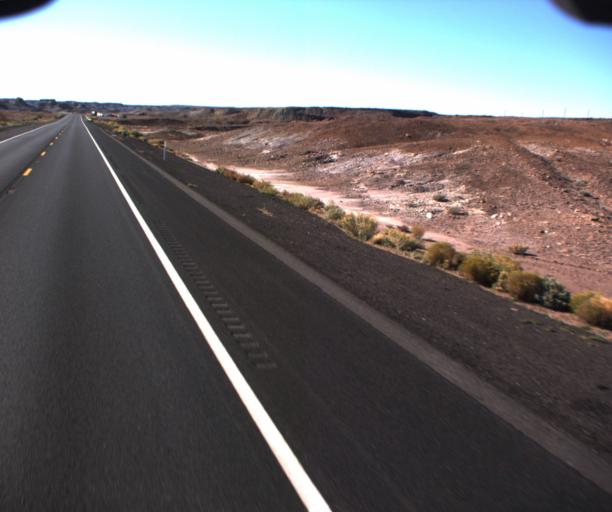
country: US
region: Arizona
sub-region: Coconino County
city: Tuba City
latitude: 36.1114
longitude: -111.3955
